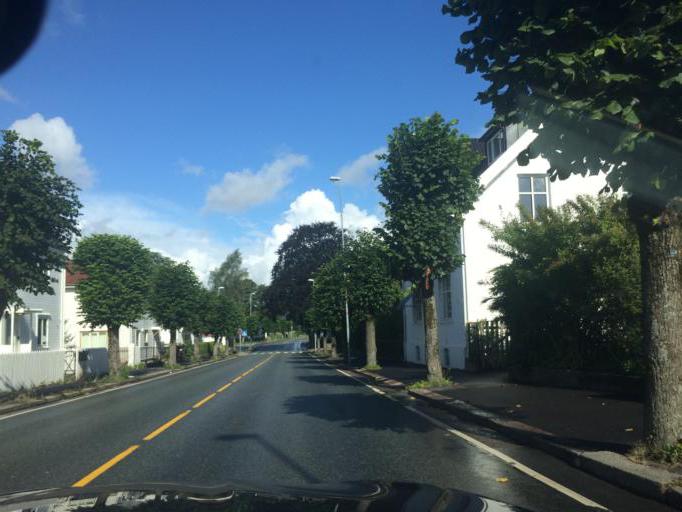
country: NO
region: Vest-Agder
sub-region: Kristiansand
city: Kristiansand
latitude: 58.1526
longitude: 8.0068
